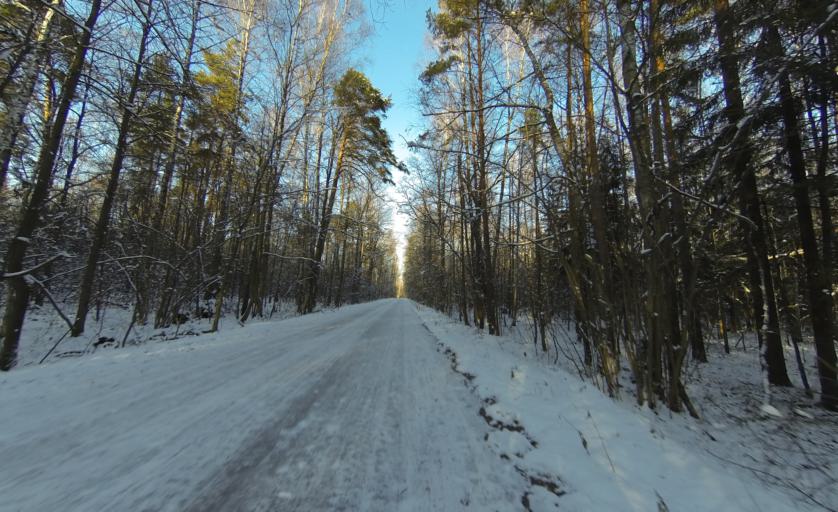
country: RU
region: Moskovskaya
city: Bogorodskoye
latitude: 55.8394
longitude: 37.7271
